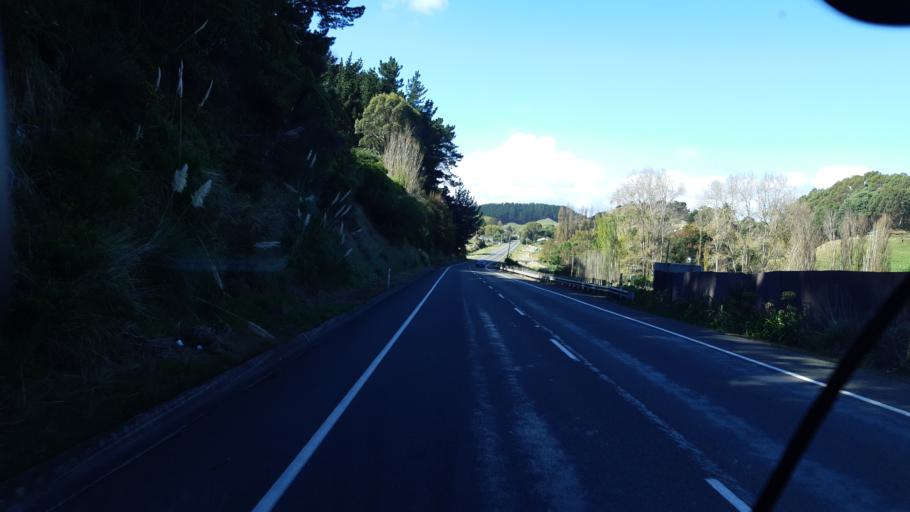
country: NZ
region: Manawatu-Wanganui
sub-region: Wanganui District
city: Wanganui
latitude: -39.9584
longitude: 175.0839
